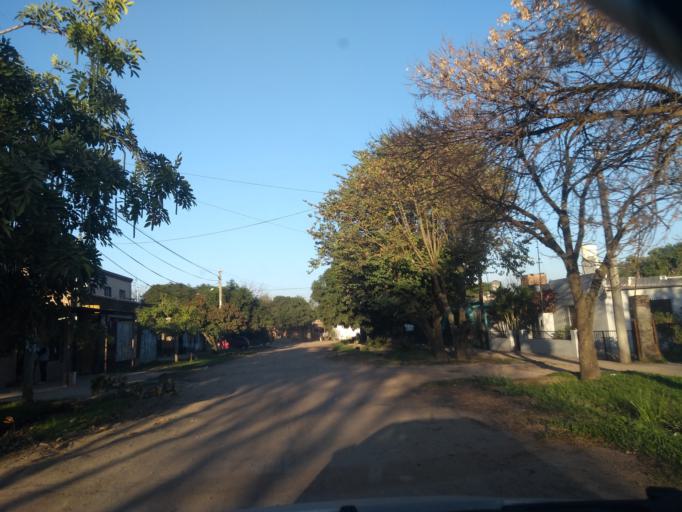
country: AR
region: Chaco
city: Barranqueras
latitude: -27.4773
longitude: -58.9613
